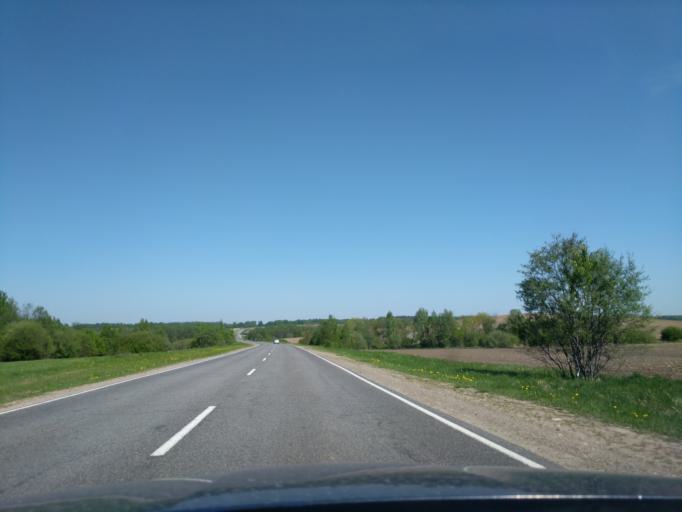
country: BY
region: Minsk
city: Il'ya
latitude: 54.2927
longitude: 27.4838
